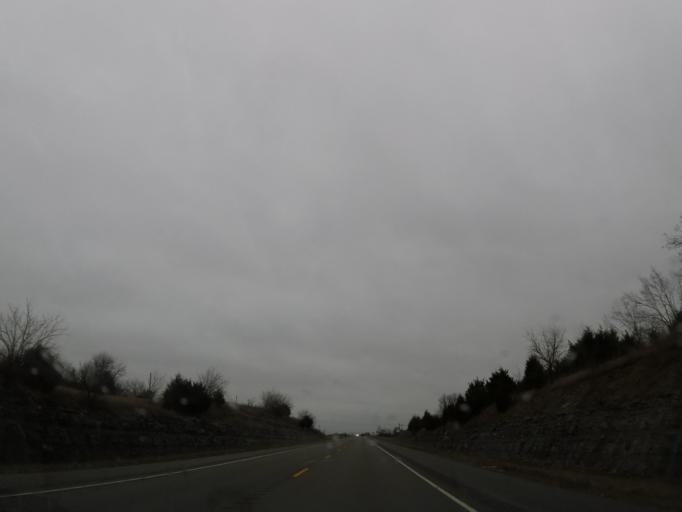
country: US
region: Kentucky
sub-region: Lincoln County
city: Stanford
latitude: 37.5219
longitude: -84.6201
